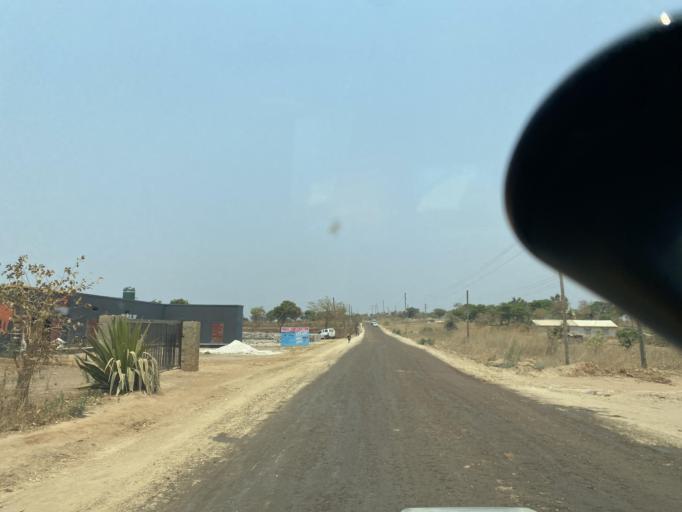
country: ZM
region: Lusaka
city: Lusaka
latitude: -15.5527
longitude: 28.3640
